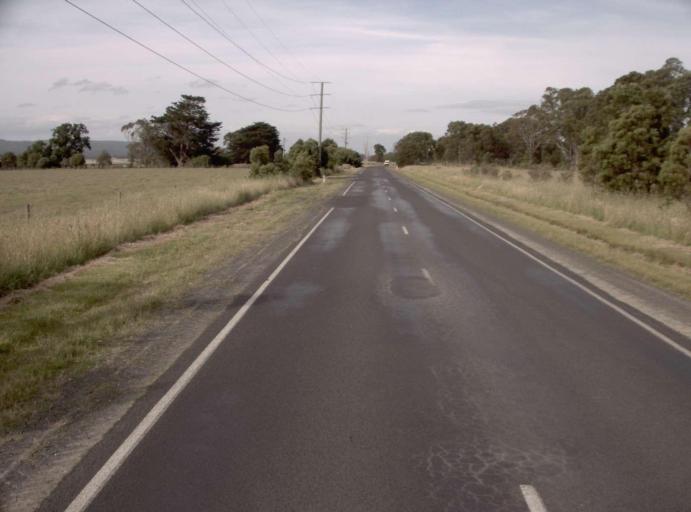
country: AU
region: Victoria
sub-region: Latrobe
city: Traralgon
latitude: -38.1001
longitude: 146.5947
